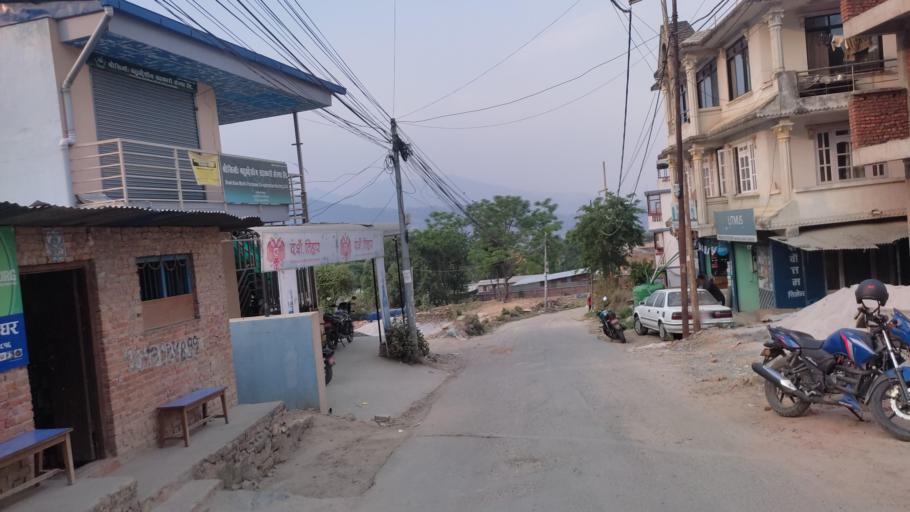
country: NP
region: Central Region
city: Kirtipur
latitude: 27.6737
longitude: 85.2447
